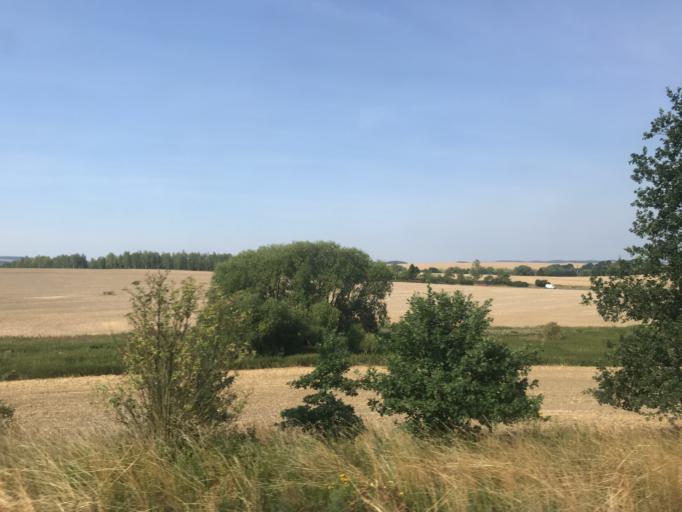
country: CZ
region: Central Bohemia
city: Bystrice
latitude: 49.7516
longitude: 14.6779
